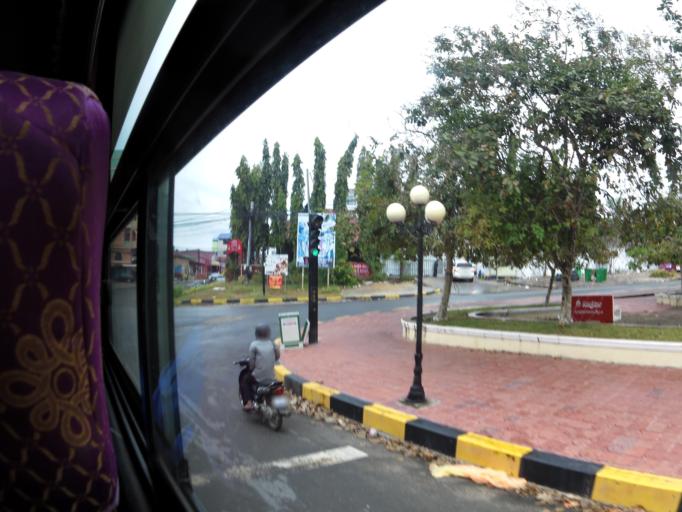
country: KH
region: Preah Sihanouk
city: Sihanoukville
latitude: 10.6308
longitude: 103.5059
